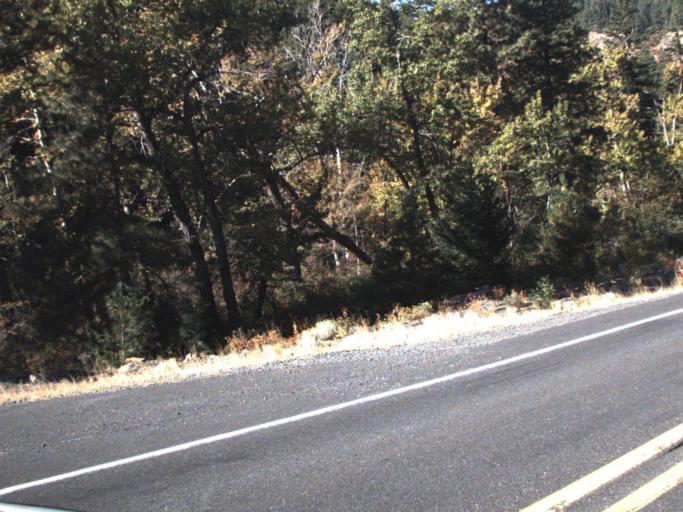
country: US
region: Washington
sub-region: Yakima County
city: Tieton
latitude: 46.6953
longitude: -120.9154
